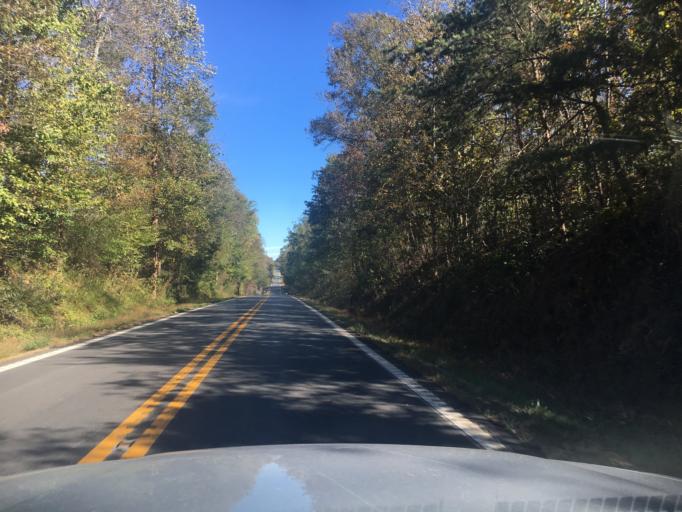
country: US
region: North Carolina
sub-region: Burke County
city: Glen Alpine
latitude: 35.5881
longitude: -81.8337
